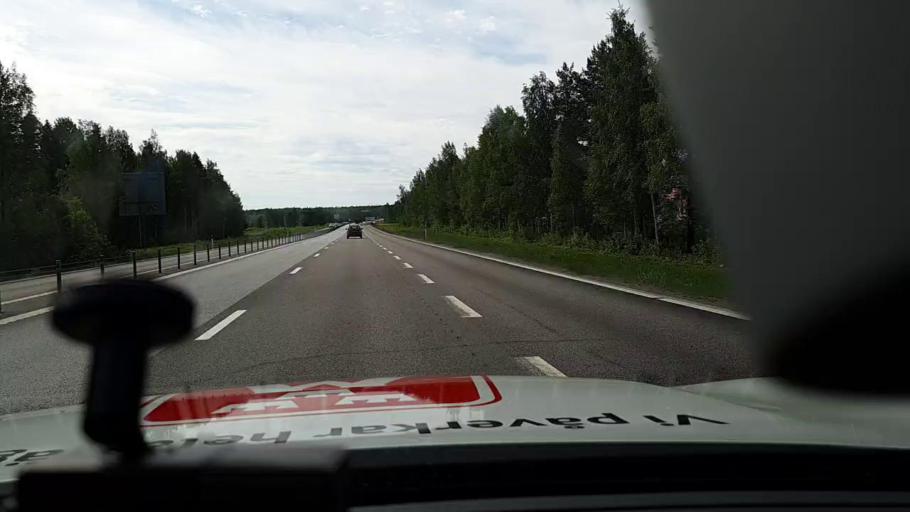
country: SE
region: Norrbotten
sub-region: Lulea Kommun
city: Gammelstad
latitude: 65.6182
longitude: 22.0571
